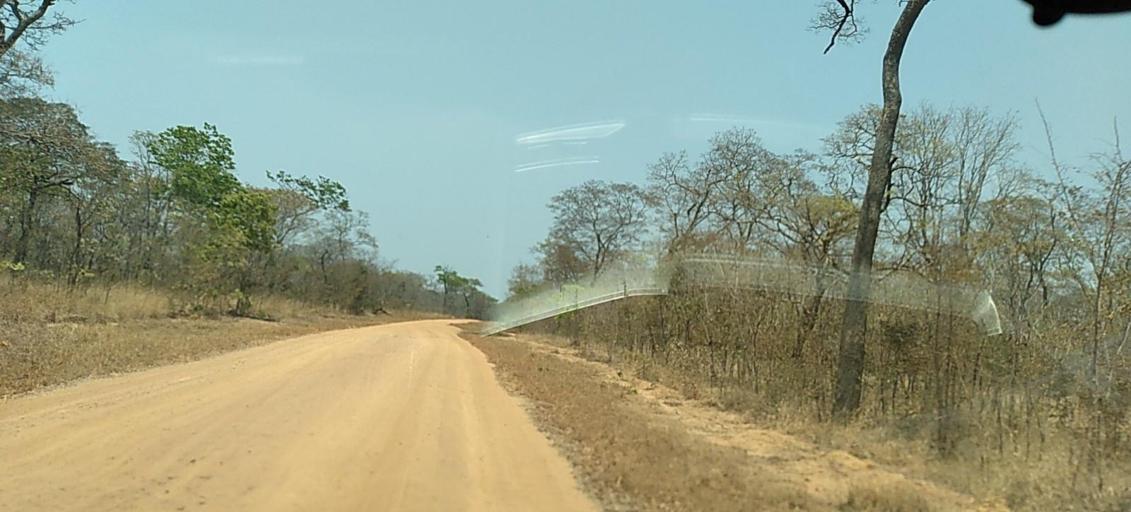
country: ZM
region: Central
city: Mumbwa
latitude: -14.3611
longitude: 26.4799
